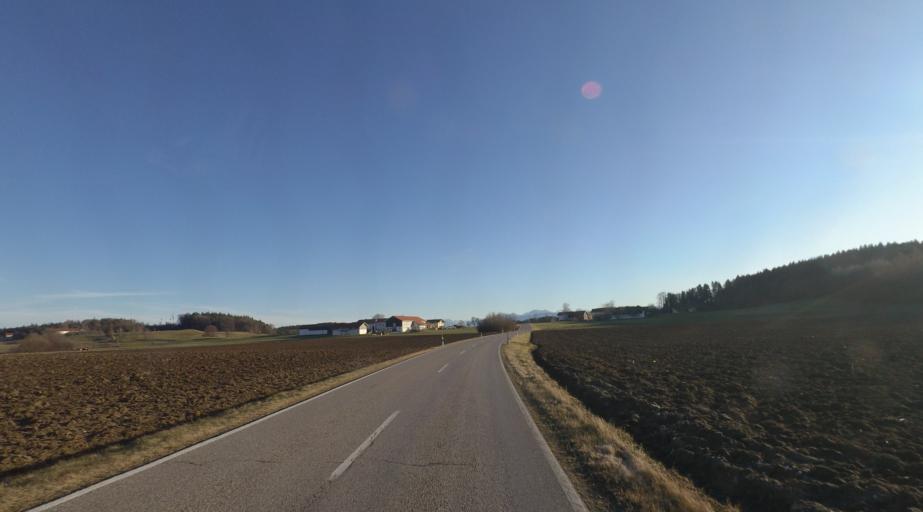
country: DE
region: Bavaria
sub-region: Upper Bavaria
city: Palling
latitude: 48.0073
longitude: 12.6900
